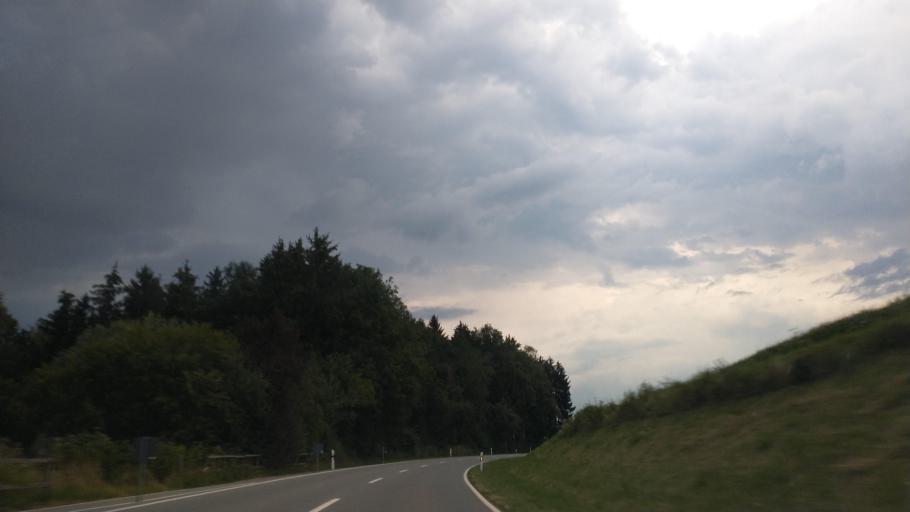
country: DE
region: Baden-Wuerttemberg
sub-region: Tuebingen Region
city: Neukirch
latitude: 47.6634
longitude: 9.7164
